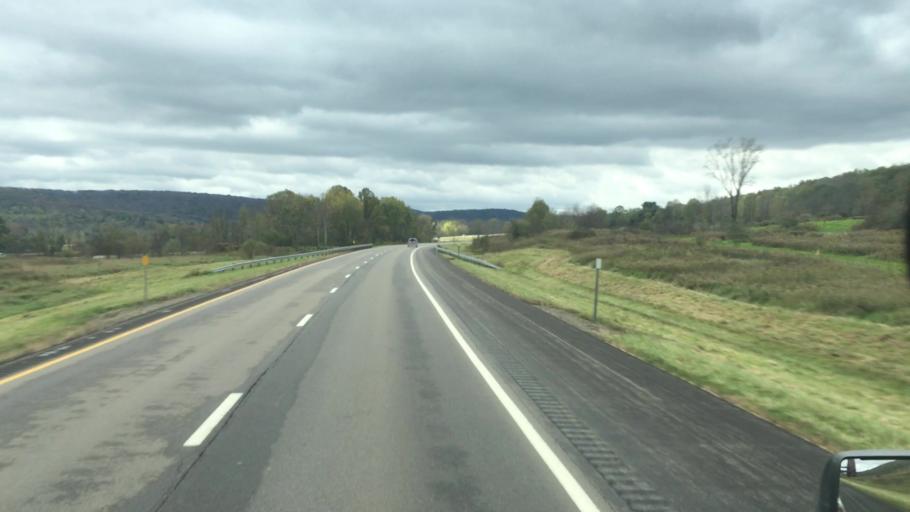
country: US
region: New York
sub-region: Allegany County
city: Friendship
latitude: 42.2325
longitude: -78.0899
